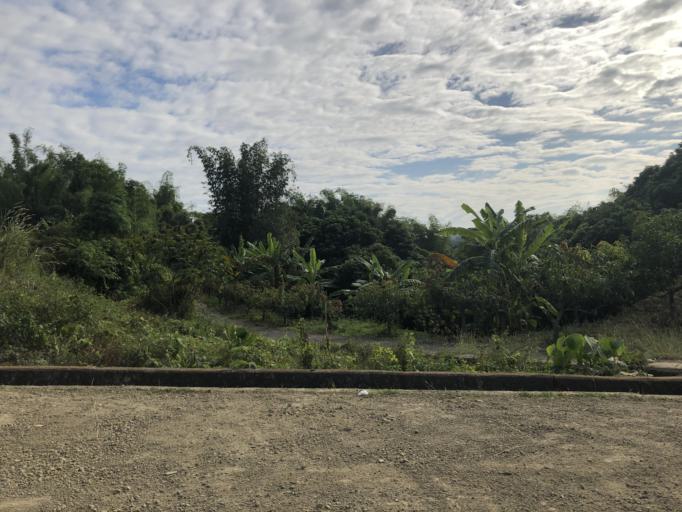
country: TW
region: Taiwan
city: Yujing
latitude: 23.0534
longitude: 120.4098
